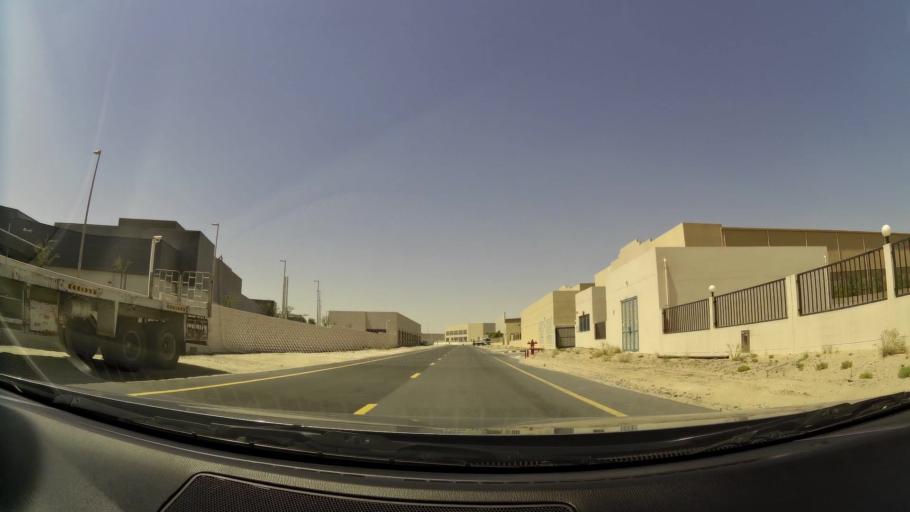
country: AE
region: Dubai
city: Dubai
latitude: 24.9761
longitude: 55.1944
